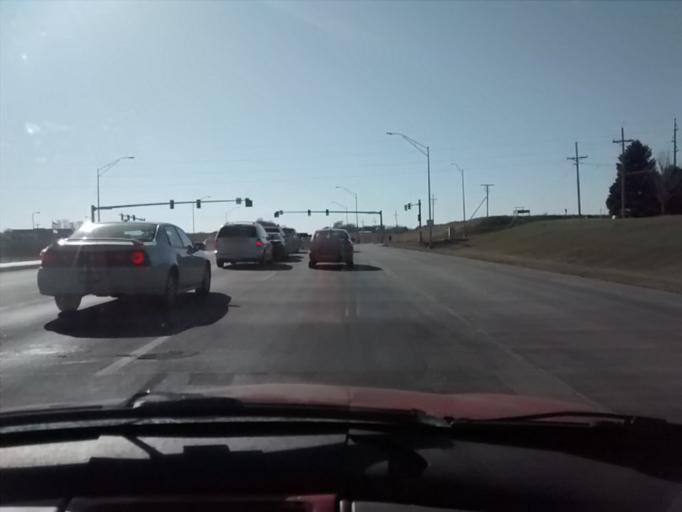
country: US
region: Nebraska
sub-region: Sarpy County
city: Papillion
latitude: 41.1403
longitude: -95.9845
